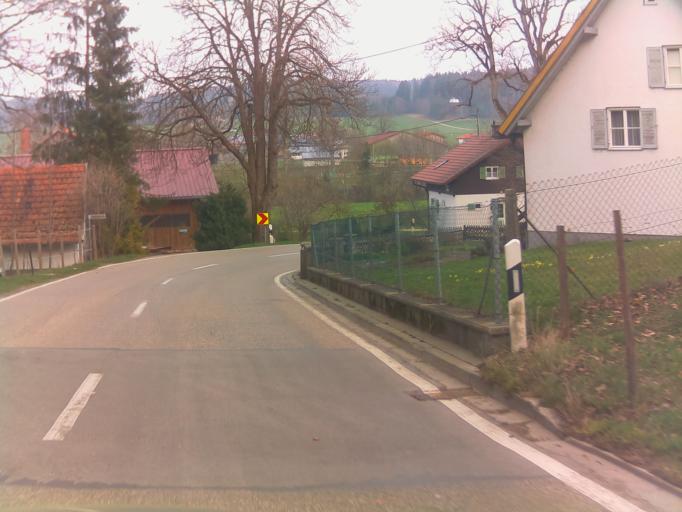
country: DE
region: Bavaria
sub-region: Swabia
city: Mauerstetten
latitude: 47.8725
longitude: 10.6861
